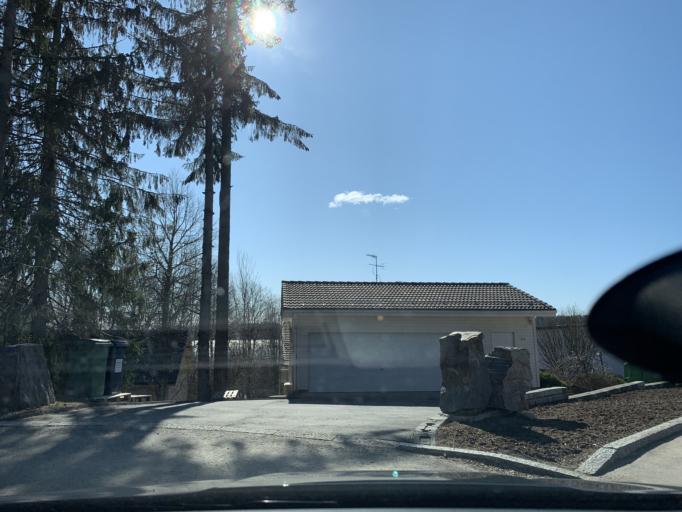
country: FI
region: Uusimaa
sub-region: Helsinki
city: Espoo
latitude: 60.1650
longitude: 24.6020
